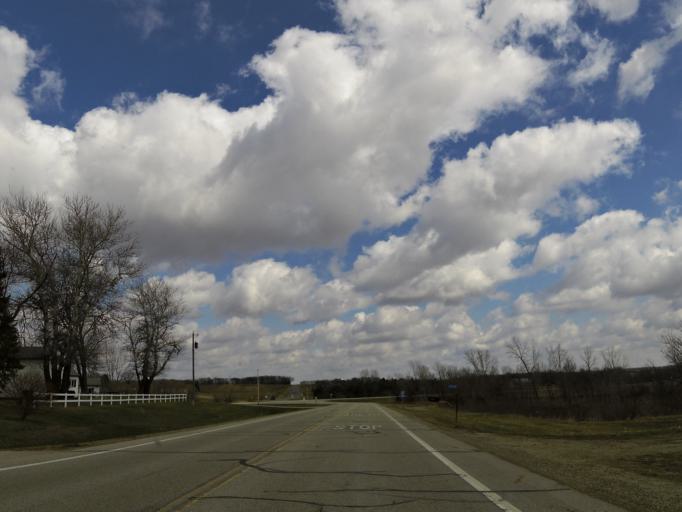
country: US
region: Minnesota
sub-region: Dodge County
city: Mantorville
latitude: 44.0800
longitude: -92.7626
